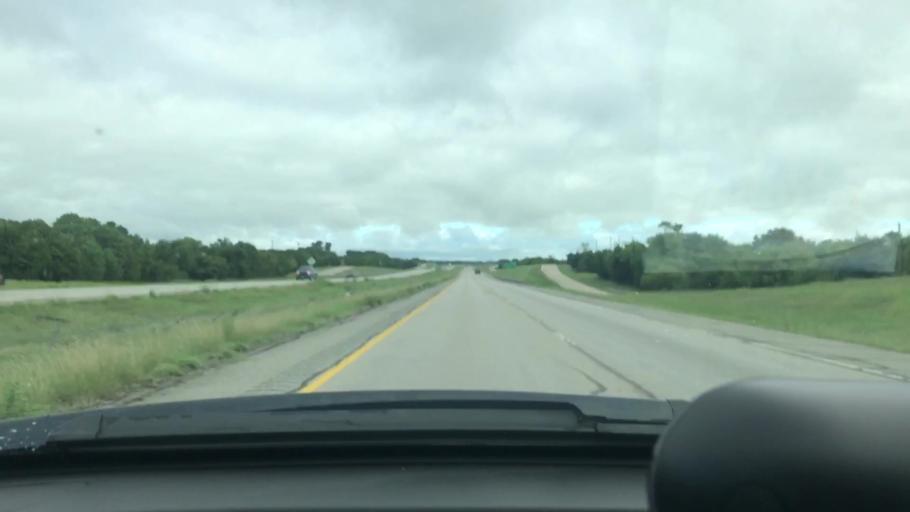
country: US
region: Texas
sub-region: Grayson County
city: Van Alstyne
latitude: 33.3867
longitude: -96.5807
